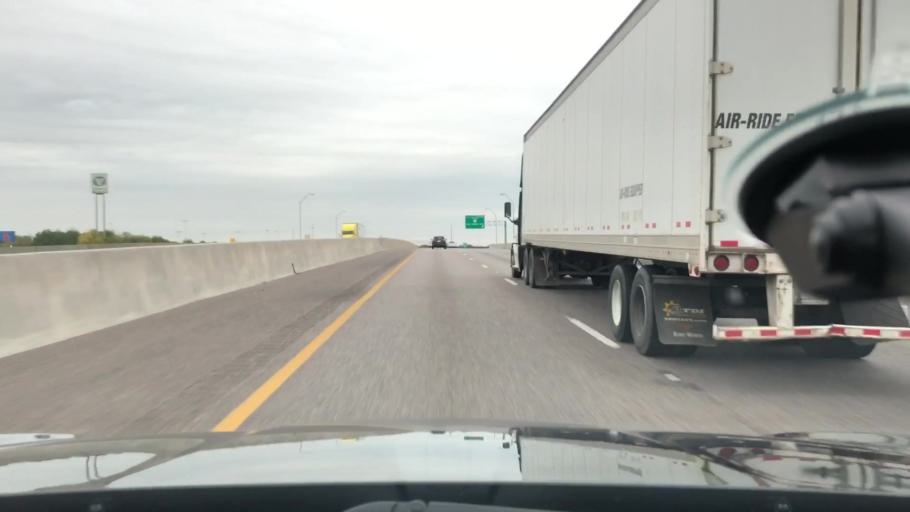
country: US
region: Texas
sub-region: McLennan County
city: Northcrest
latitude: 31.6382
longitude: -97.0961
